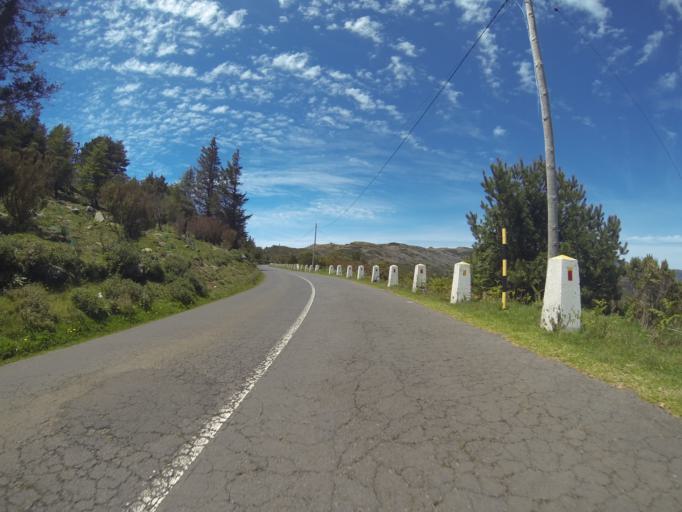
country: PT
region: Madeira
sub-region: Funchal
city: Nossa Senhora do Monte
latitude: 32.7122
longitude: -16.8989
